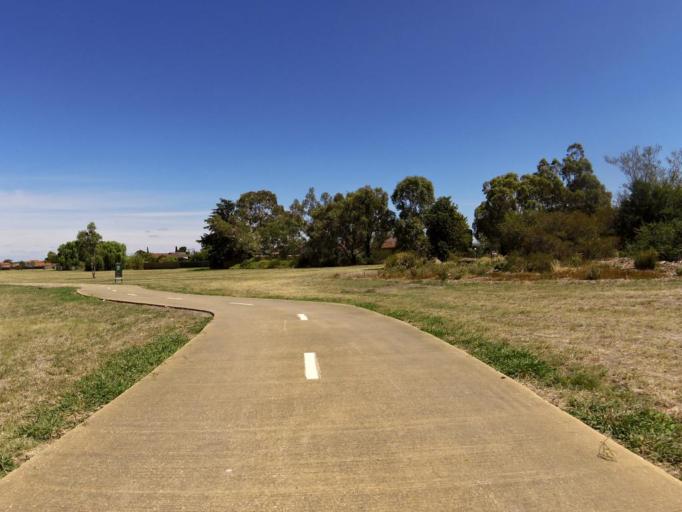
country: AU
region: Victoria
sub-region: Hume
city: Campbellfield
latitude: -37.6736
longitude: 144.9731
